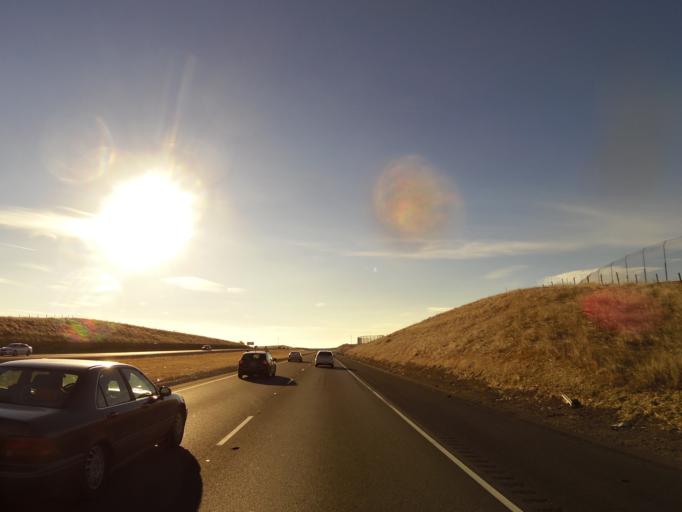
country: US
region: California
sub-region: Stanislaus County
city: Patterson
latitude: 37.3923
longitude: -121.1349
